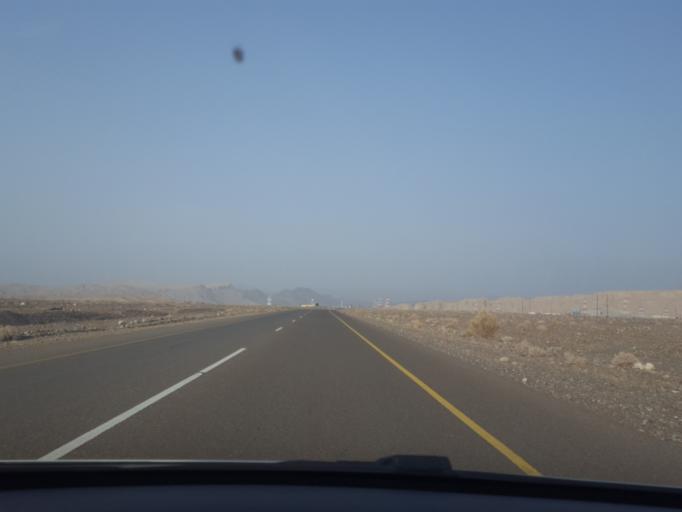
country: AE
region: Abu Dhabi
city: Al Ain
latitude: 24.0314
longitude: 55.9969
